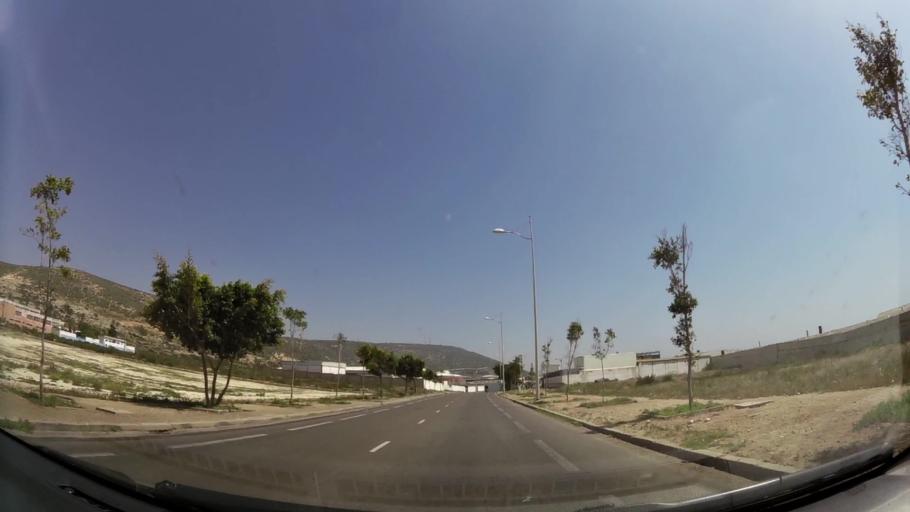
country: MA
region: Souss-Massa-Draa
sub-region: Agadir-Ida-ou-Tnan
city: Aourir
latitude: 30.4443
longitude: -9.6499
